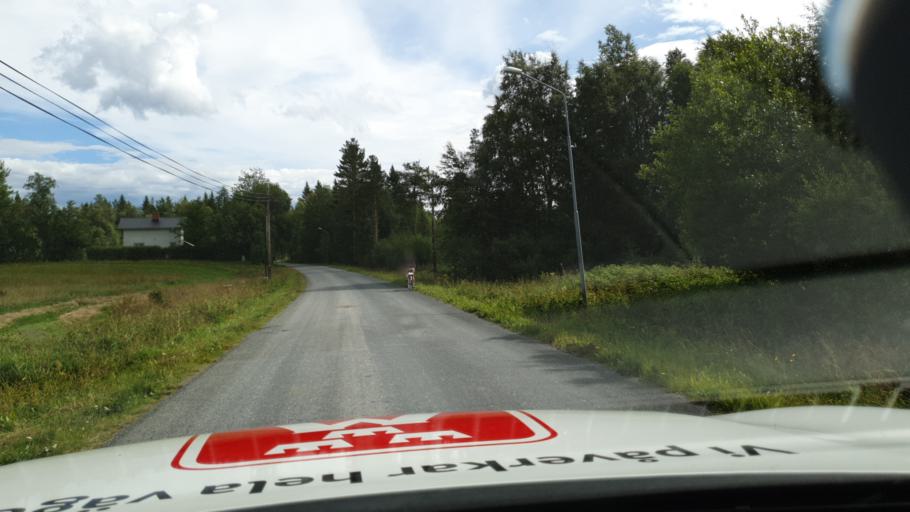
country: SE
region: Jaemtland
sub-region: Krokoms Kommun
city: Valla
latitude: 63.2719
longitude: 13.9159
